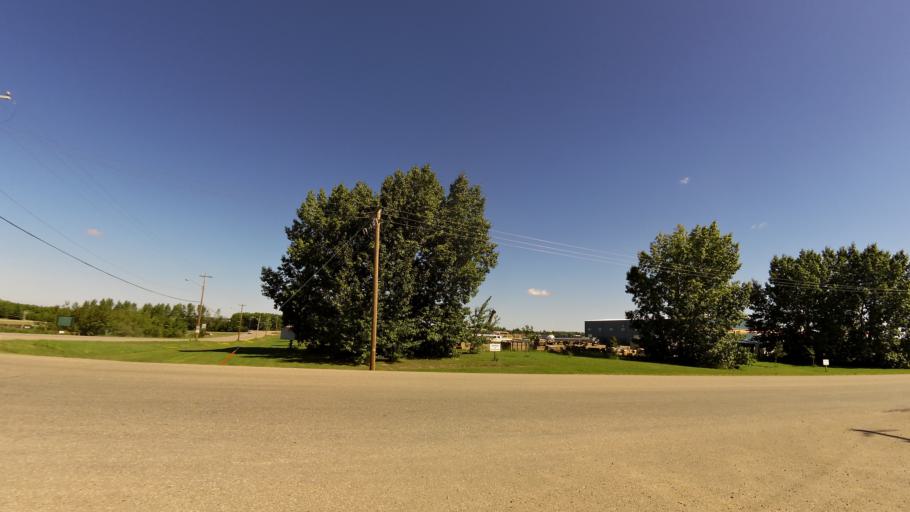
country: CA
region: Alberta
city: Wainwright
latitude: 52.8324
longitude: -110.8784
